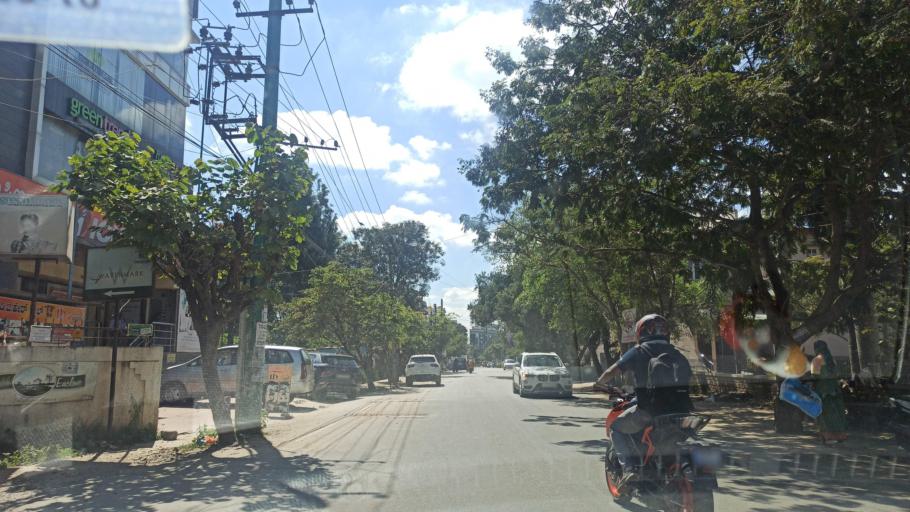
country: IN
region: Karnataka
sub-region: Bangalore Urban
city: Bangalore
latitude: 12.9158
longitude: 77.6675
